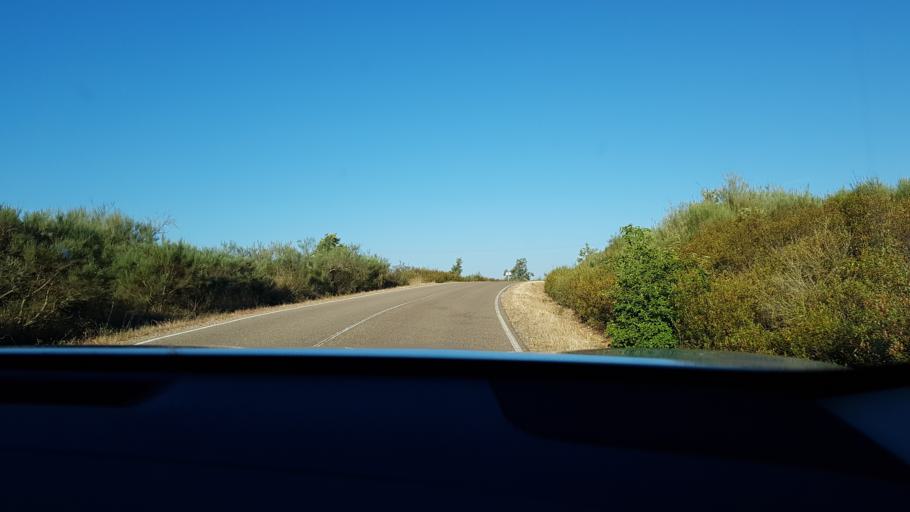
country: ES
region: Castille and Leon
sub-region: Provincia de Zamora
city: Samir de los Canos
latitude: 41.6642
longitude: -6.1770
